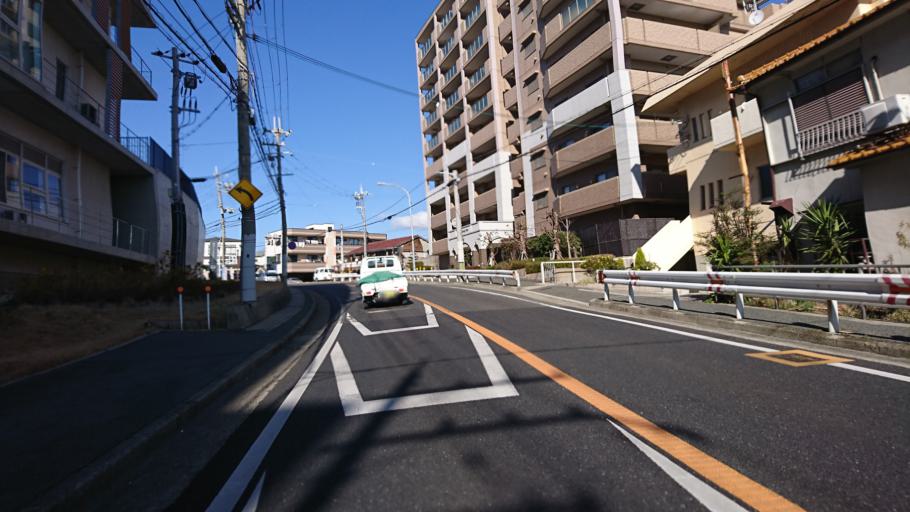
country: JP
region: Hyogo
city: Akashi
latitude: 34.6609
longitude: 134.9501
